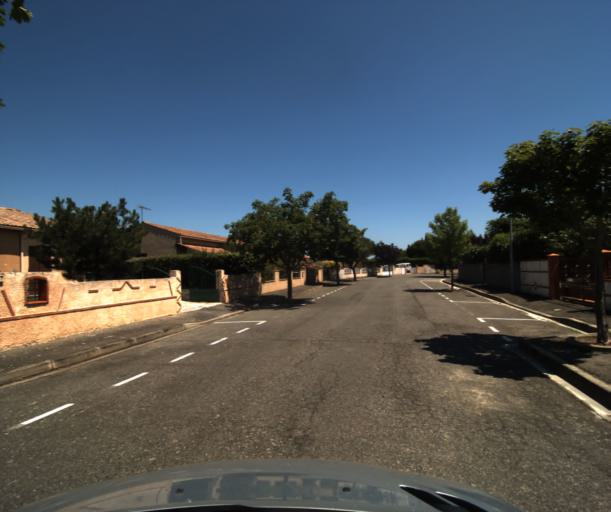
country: FR
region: Midi-Pyrenees
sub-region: Departement de la Haute-Garonne
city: Roquettes
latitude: 43.4967
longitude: 1.3773
